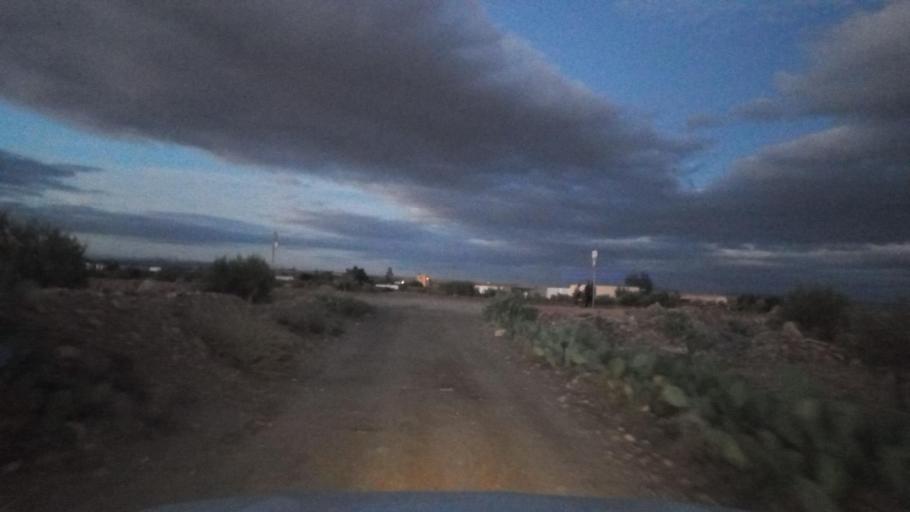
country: TN
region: Al Qasrayn
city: Kasserine
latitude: 35.2575
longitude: 8.9416
